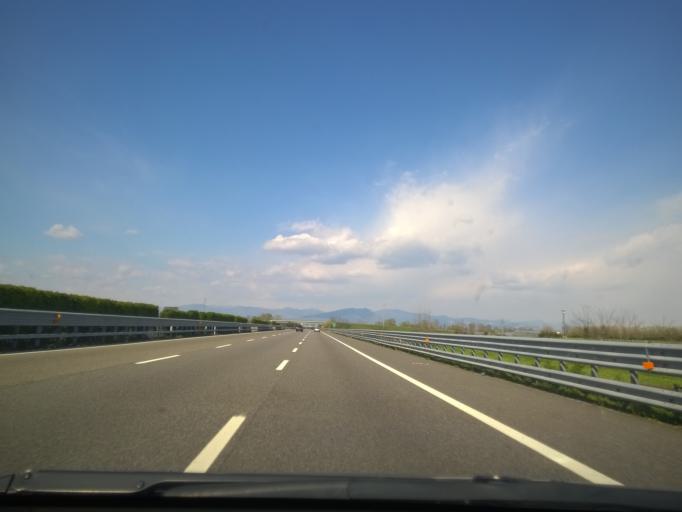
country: IT
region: Lombardy
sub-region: Provincia di Brescia
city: Bagnolo Mella
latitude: 45.4028
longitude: 10.1889
